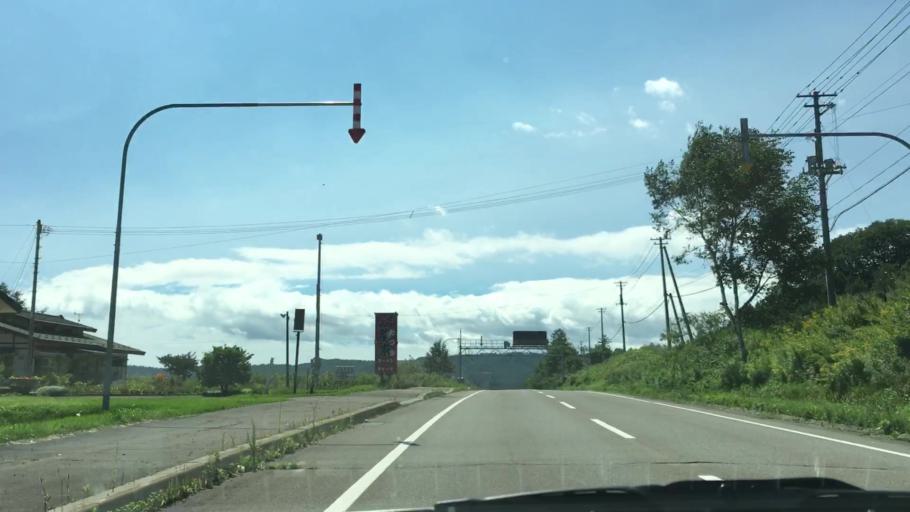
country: JP
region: Hokkaido
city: Otofuke
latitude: 43.2510
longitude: 143.5646
